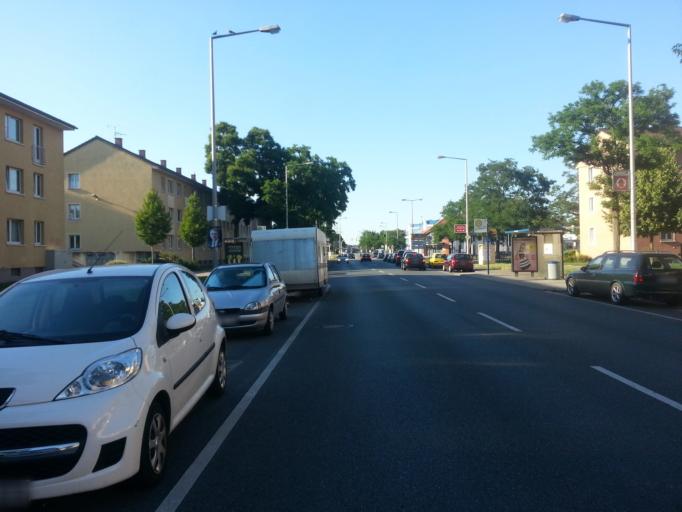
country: DE
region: Baden-Wuerttemberg
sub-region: Karlsruhe Region
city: Mannheim
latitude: 49.5127
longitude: 8.5082
